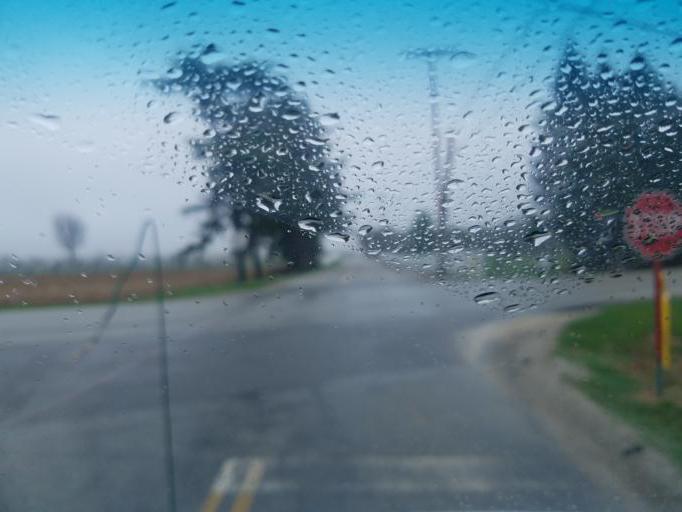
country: US
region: Ohio
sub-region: Wood County
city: North Baltimore
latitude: 41.1443
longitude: -83.6312
